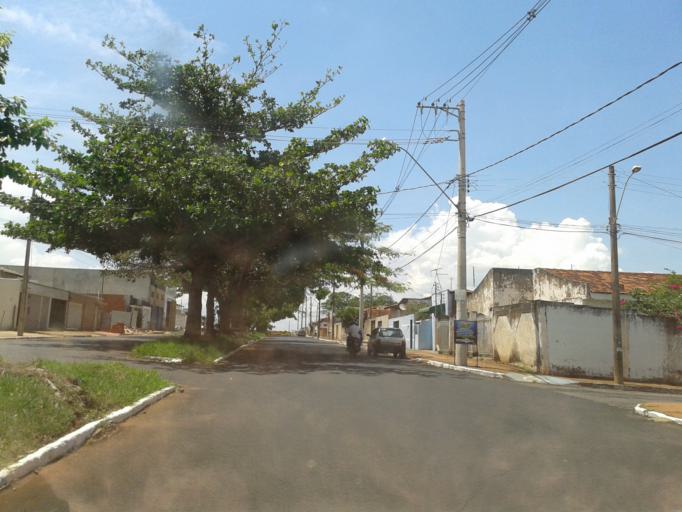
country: BR
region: Minas Gerais
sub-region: Araguari
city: Araguari
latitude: -18.6704
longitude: -48.1965
